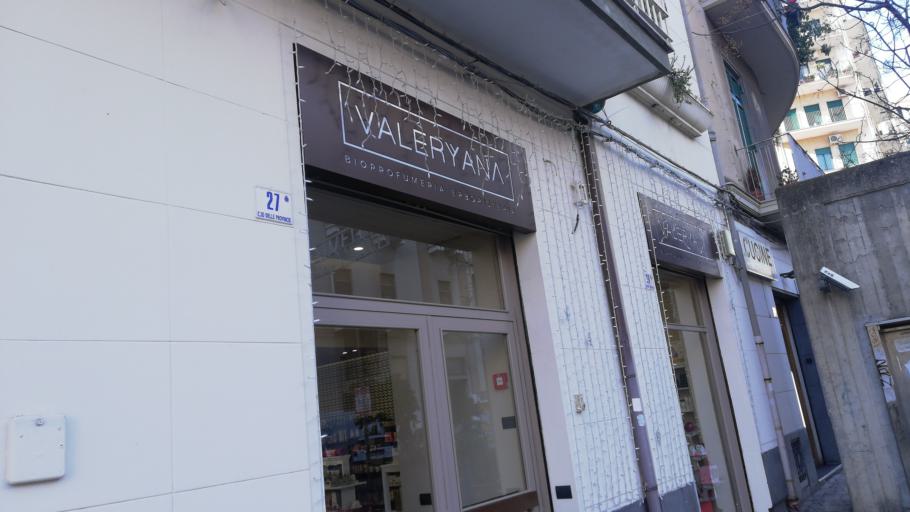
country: IT
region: Sicily
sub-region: Catania
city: Canalicchio
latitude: 37.5161
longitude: 15.0965
